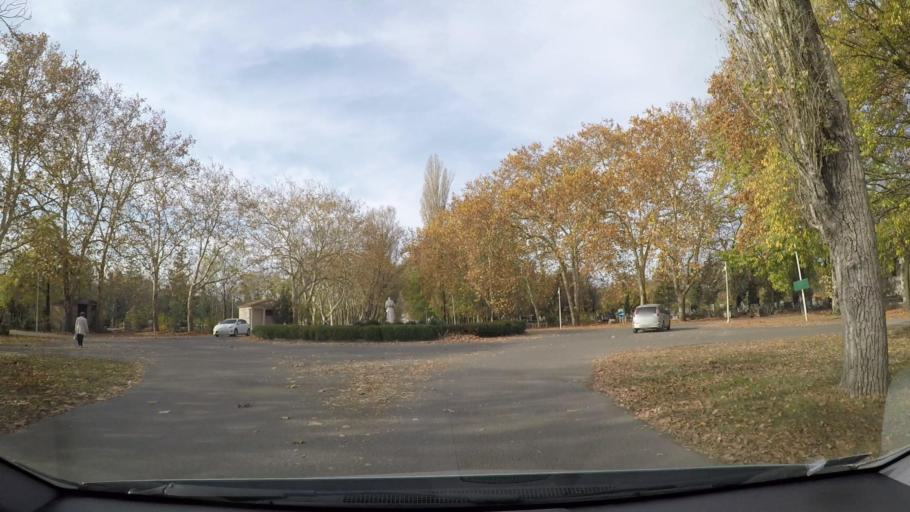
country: HU
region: Budapest
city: Budapest X. keruelet
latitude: 47.4724
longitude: 19.1851
